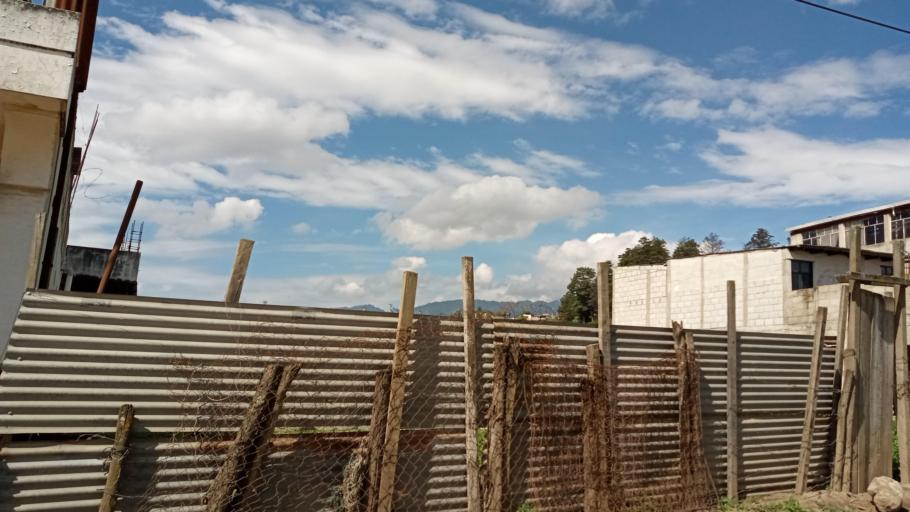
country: GT
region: Quetzaltenango
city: Quetzaltenango
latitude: 14.8449
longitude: -91.5083
